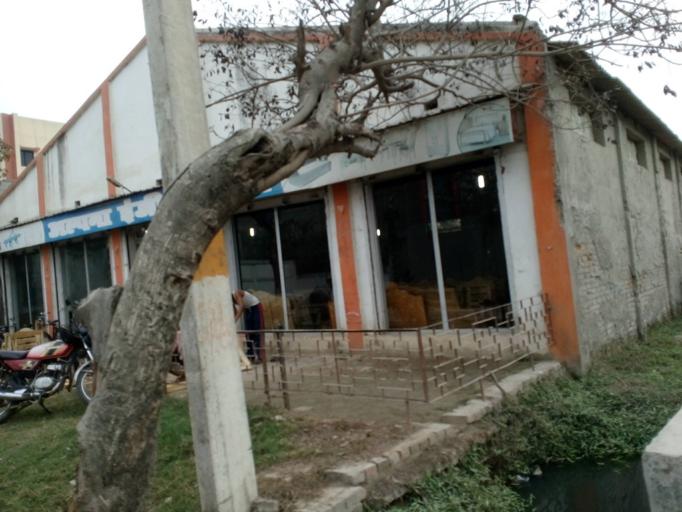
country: IN
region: Bihar
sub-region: Muzaffarpur
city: Muzaffarpur
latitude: 26.1012
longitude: 85.4073
